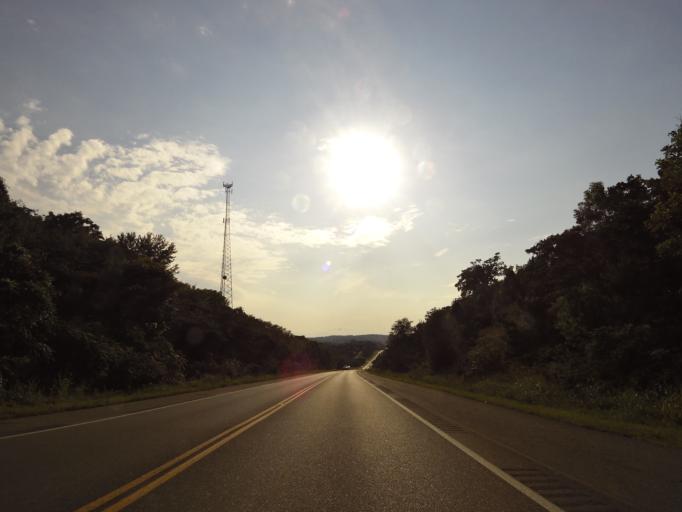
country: US
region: Tennessee
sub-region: Monroe County
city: Sweetwater
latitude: 35.6077
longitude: -84.4247
